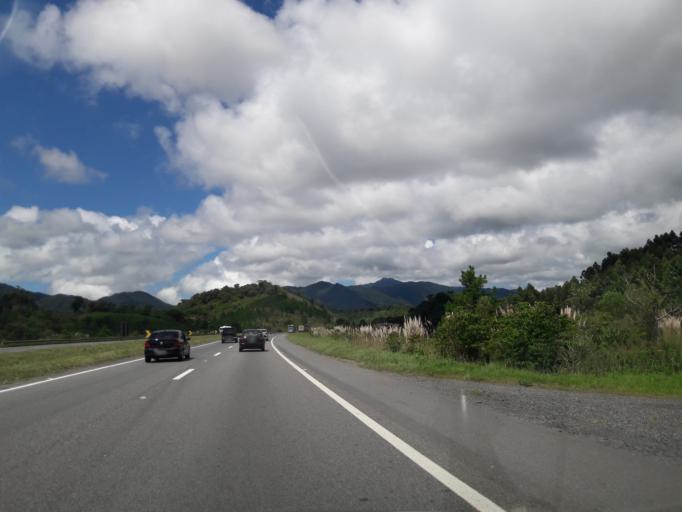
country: BR
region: Parana
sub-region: Antonina
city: Antonina
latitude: -25.0073
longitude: -48.5077
